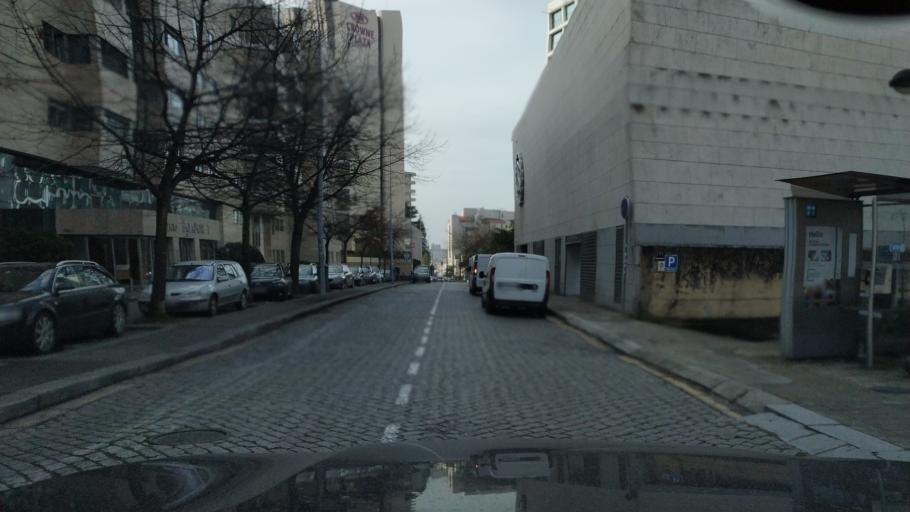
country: PT
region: Porto
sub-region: Matosinhos
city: Senhora da Hora
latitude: 41.1612
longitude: -8.6393
